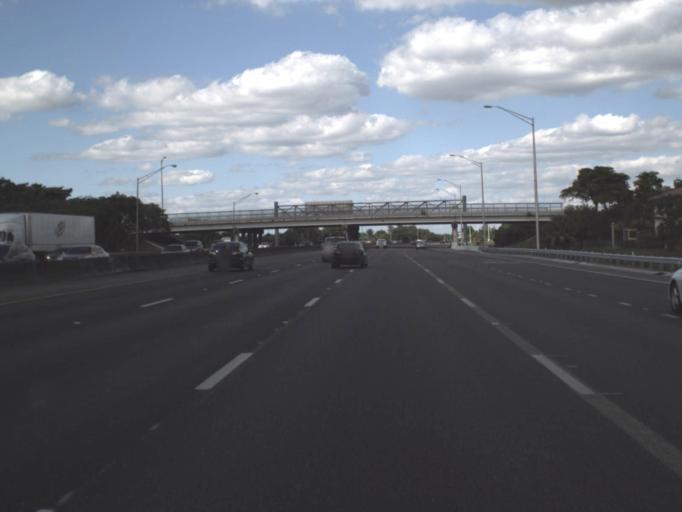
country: US
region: Florida
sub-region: Broward County
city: Miramar
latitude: 25.9798
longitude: -80.2299
